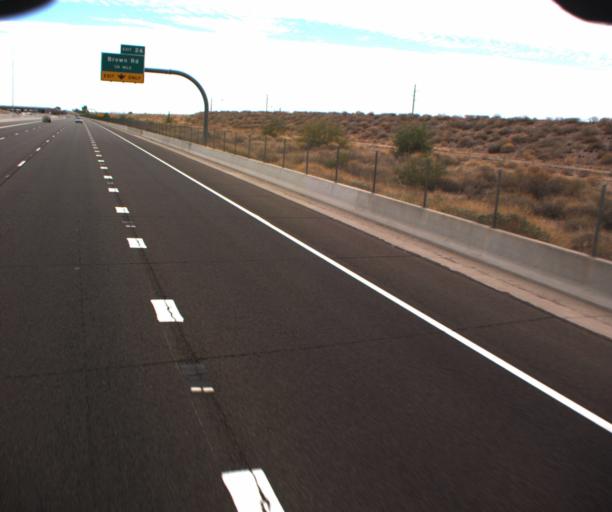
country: US
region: Arizona
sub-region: Pinal County
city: Apache Junction
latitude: 33.4440
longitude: -111.6614
